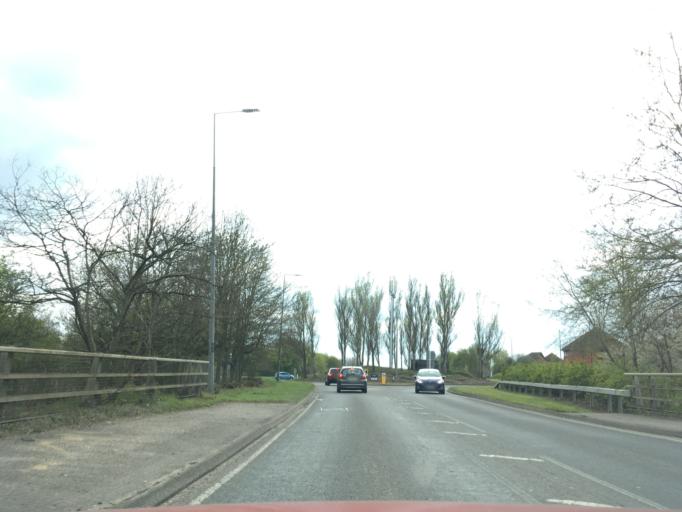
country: GB
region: England
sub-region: Milton Keynes
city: Loughton
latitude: 52.0198
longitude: -0.7667
